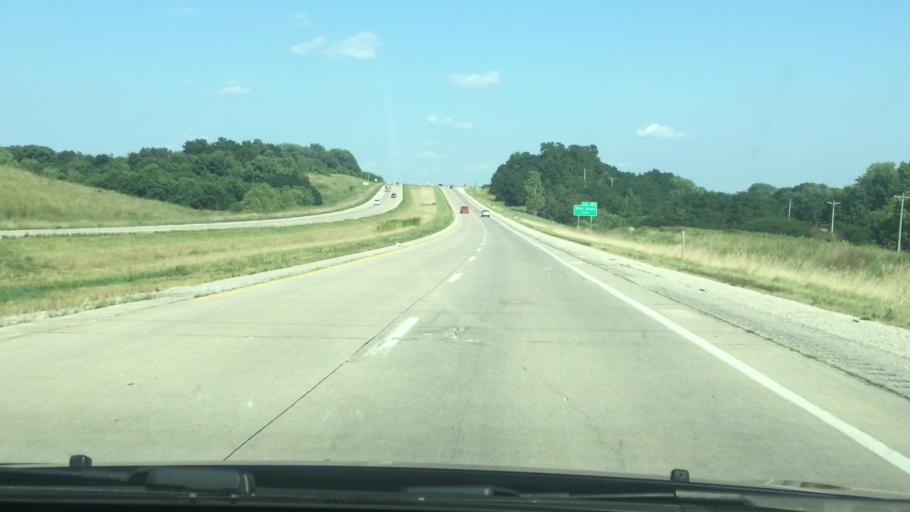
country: US
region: Iowa
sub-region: Scott County
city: Blue Grass
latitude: 41.5129
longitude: -90.8039
